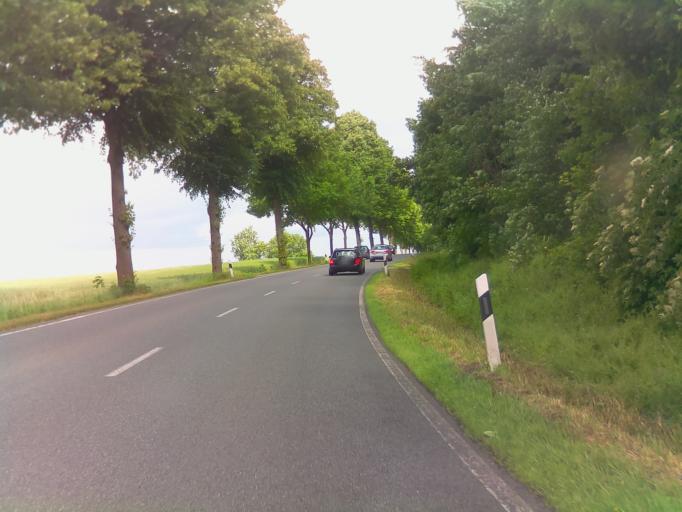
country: DE
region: Lower Saxony
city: Springe
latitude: 52.1761
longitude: 9.6166
